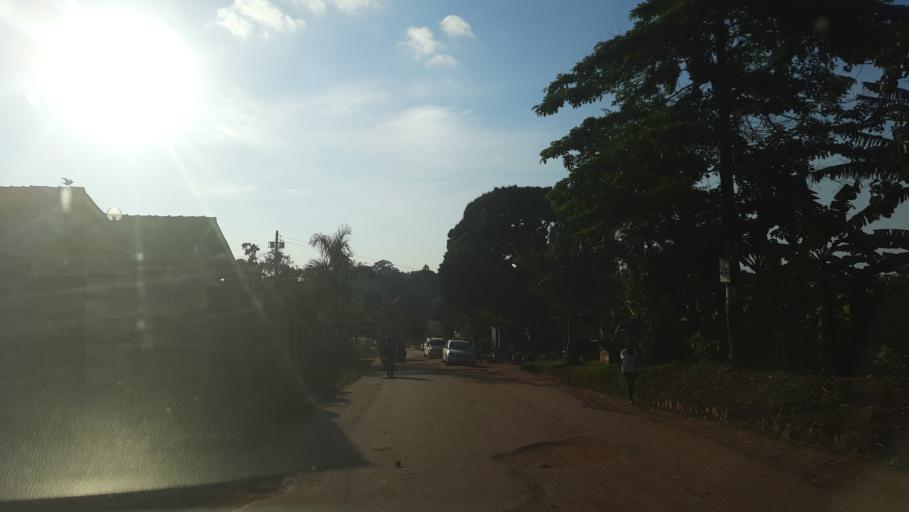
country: UG
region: Central Region
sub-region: Mukono District
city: Mukono
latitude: 0.3707
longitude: 32.7533
